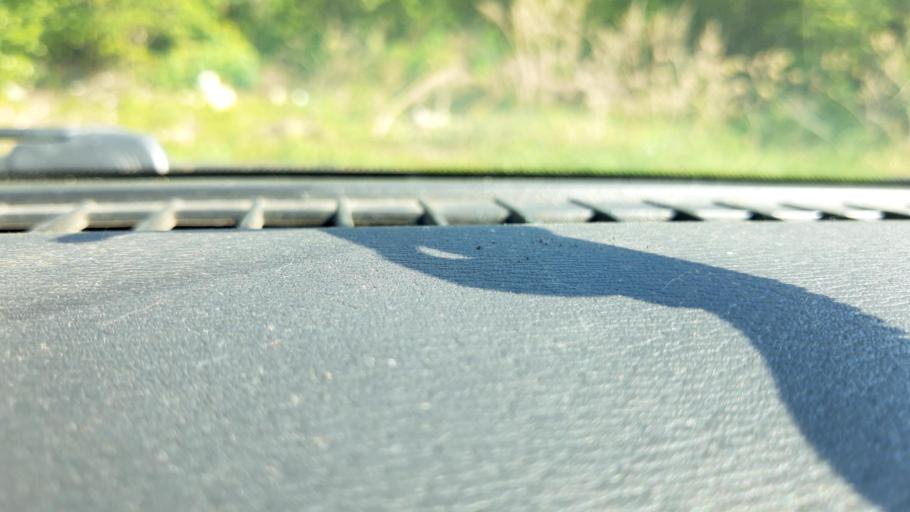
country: RU
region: Bashkortostan
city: Iglino
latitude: 54.7718
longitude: 56.2109
